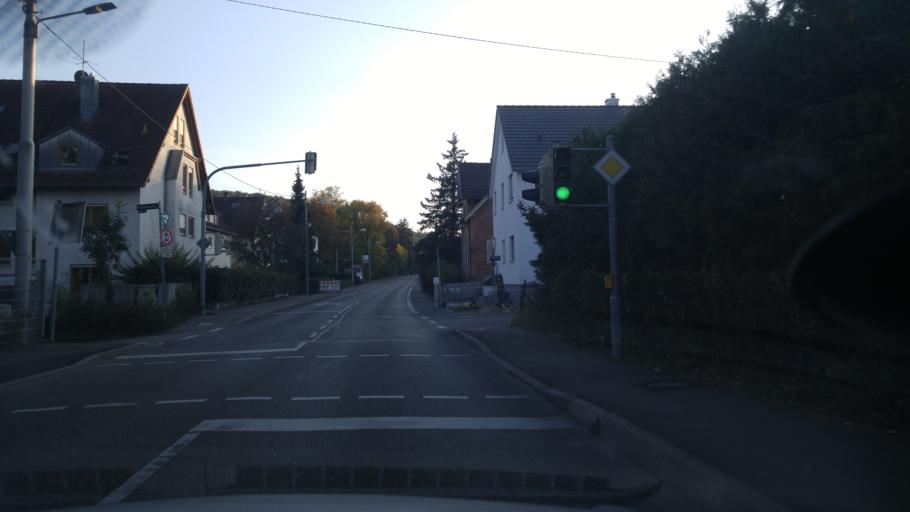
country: DE
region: Baden-Wuerttemberg
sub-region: Regierungsbezirk Stuttgart
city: Stuttgart Feuerbach
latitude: 48.7992
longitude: 9.1521
